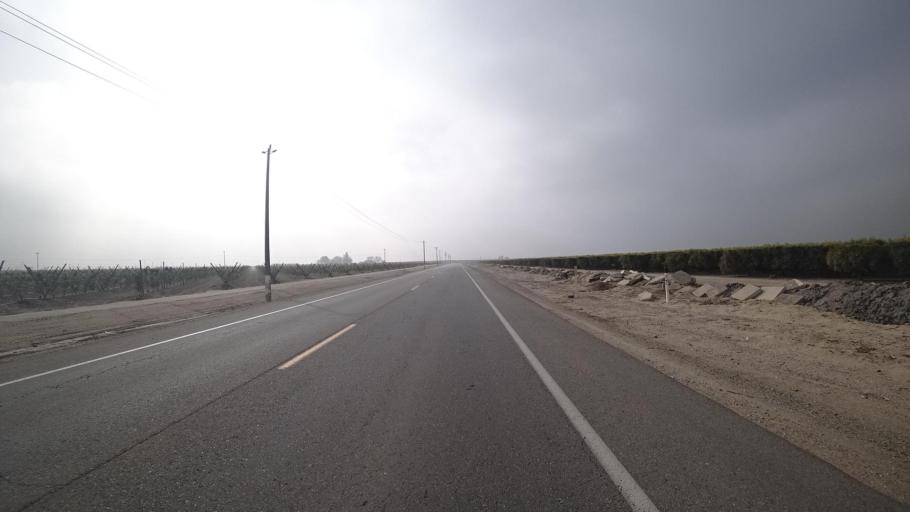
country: US
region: California
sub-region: Kern County
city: Pine Mountain Club
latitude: 35.0646
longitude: -119.1349
